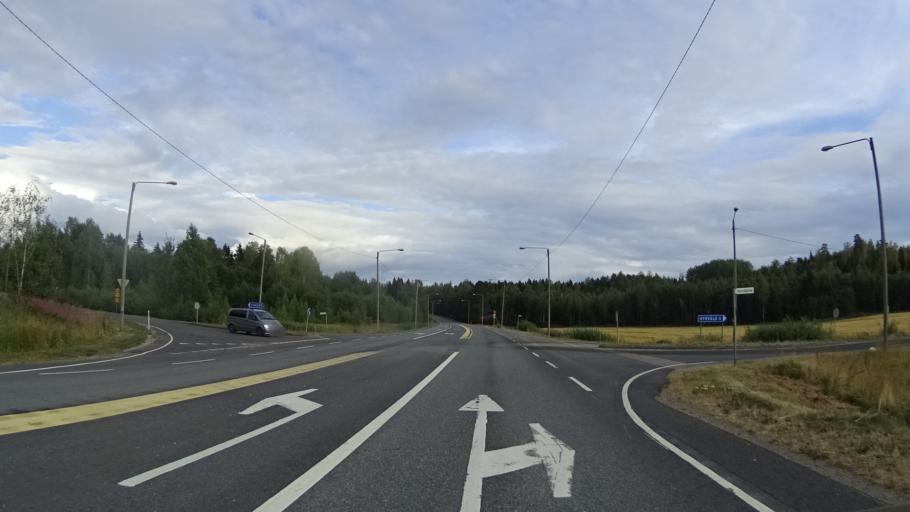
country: FI
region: Haeme
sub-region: Haemeenlinna
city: Parola
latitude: 61.0293
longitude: 24.2791
